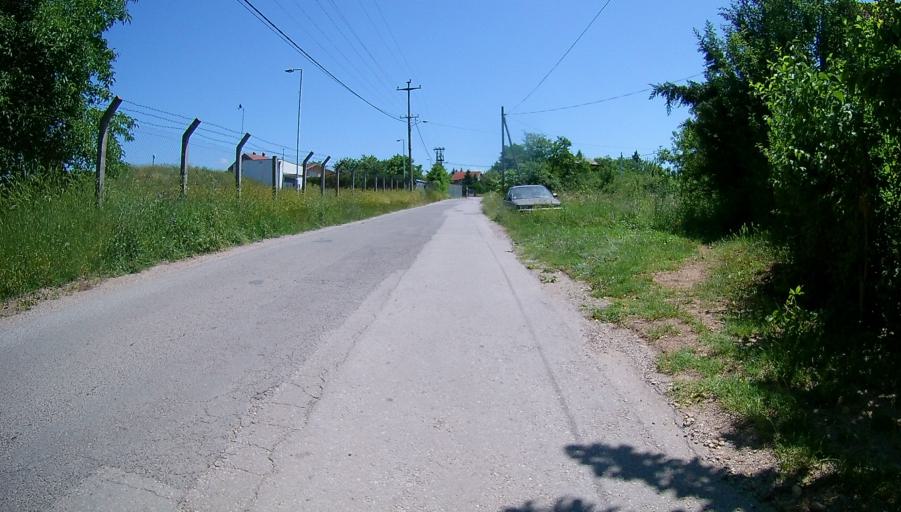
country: RS
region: Central Serbia
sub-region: Nisavski Okrug
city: Nis
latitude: 43.2942
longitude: 21.8995
